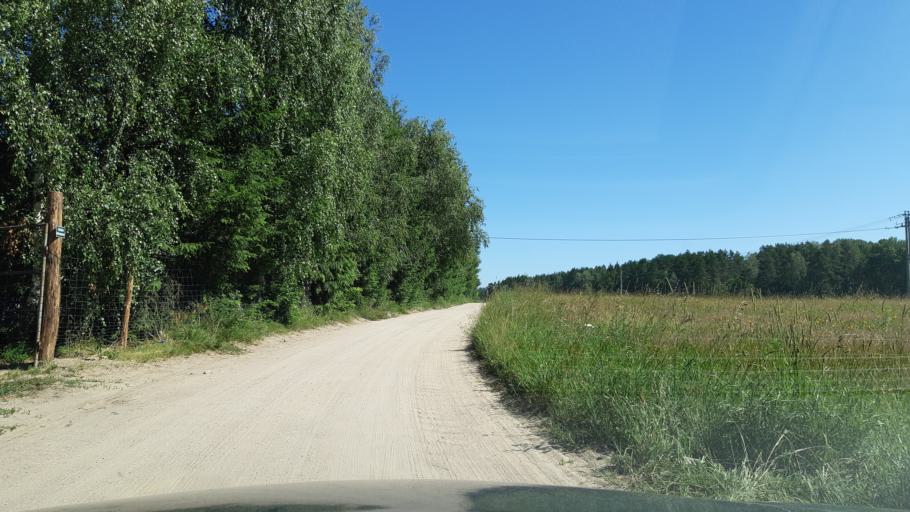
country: PL
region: Warmian-Masurian Voivodeship
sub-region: Powiat piski
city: Ruciane-Nida
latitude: 53.7081
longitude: 21.4844
